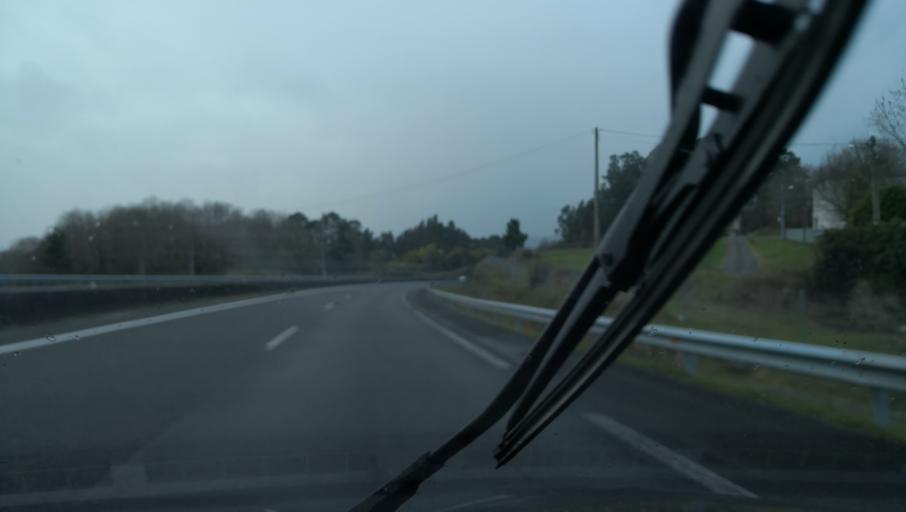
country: ES
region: Galicia
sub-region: Provincia da Coruna
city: Ribeira
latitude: 42.7475
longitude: -8.3851
